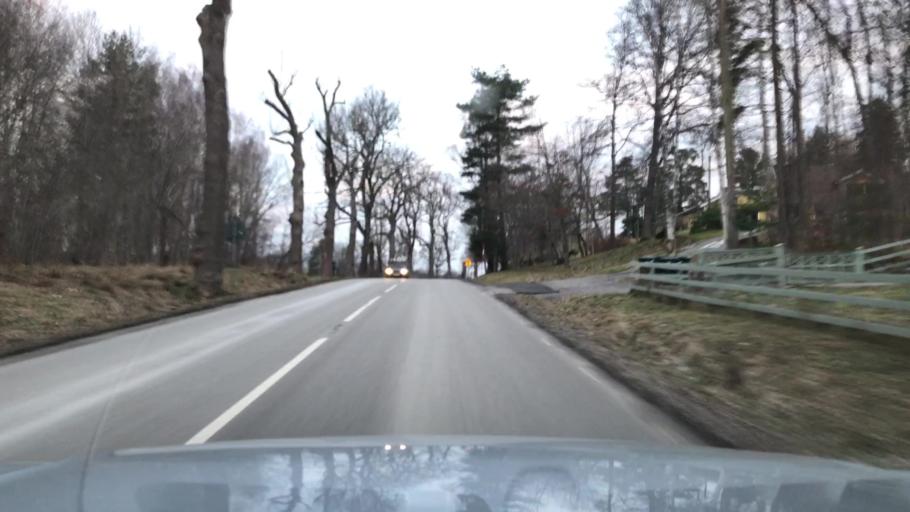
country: SE
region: OEstergoetland
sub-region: Norrkopings Kommun
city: Kimstad
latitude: 58.5172
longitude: 15.9731
